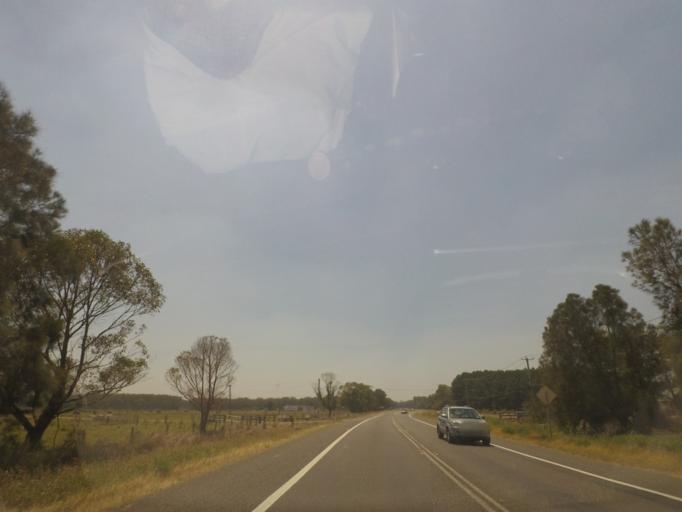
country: AU
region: New South Wales
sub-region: Port Stephens Shire
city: Medowie
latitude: -32.7947
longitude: 151.8946
